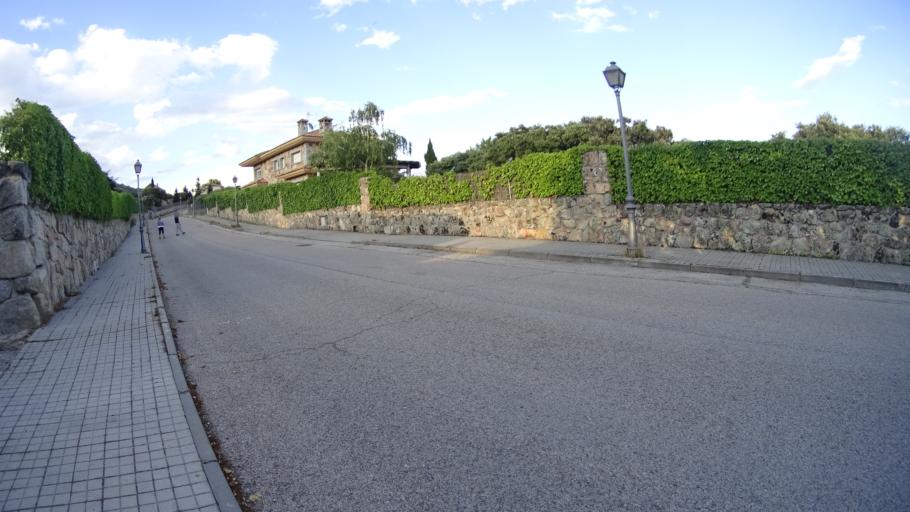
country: ES
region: Madrid
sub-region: Provincia de Madrid
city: Hoyo de Manzanares
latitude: 40.6262
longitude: -3.9141
